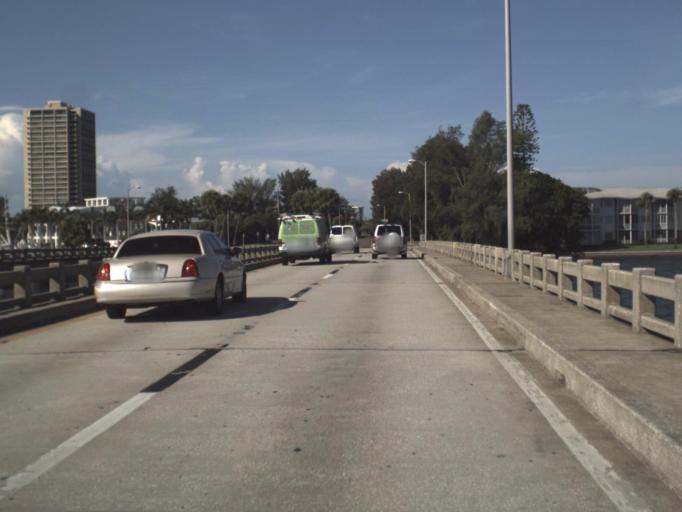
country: US
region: Florida
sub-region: Sarasota County
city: Siesta Key
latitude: 27.3245
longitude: -82.5664
